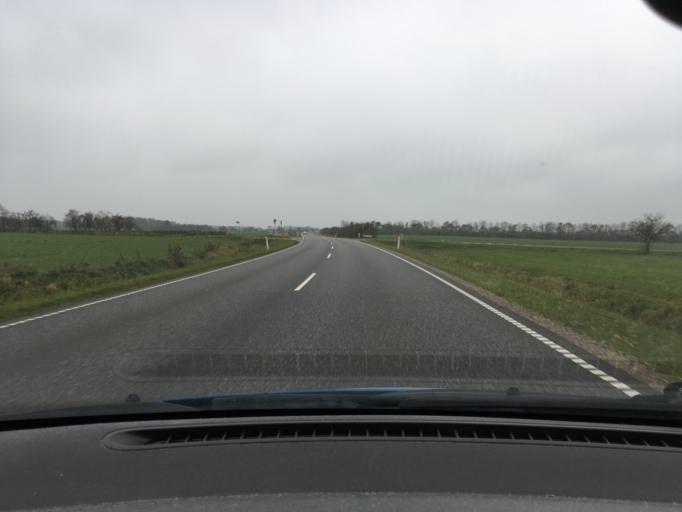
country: DK
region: South Denmark
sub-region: Tonder Kommune
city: Toftlund
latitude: 55.0550
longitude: 9.1085
